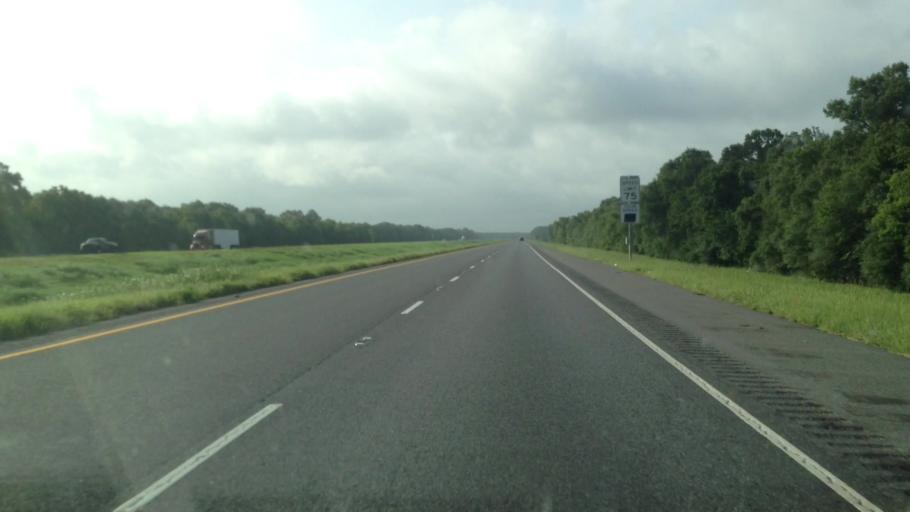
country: US
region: Louisiana
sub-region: Evangeline Parish
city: Ville Platte
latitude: 30.7124
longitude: -92.1016
